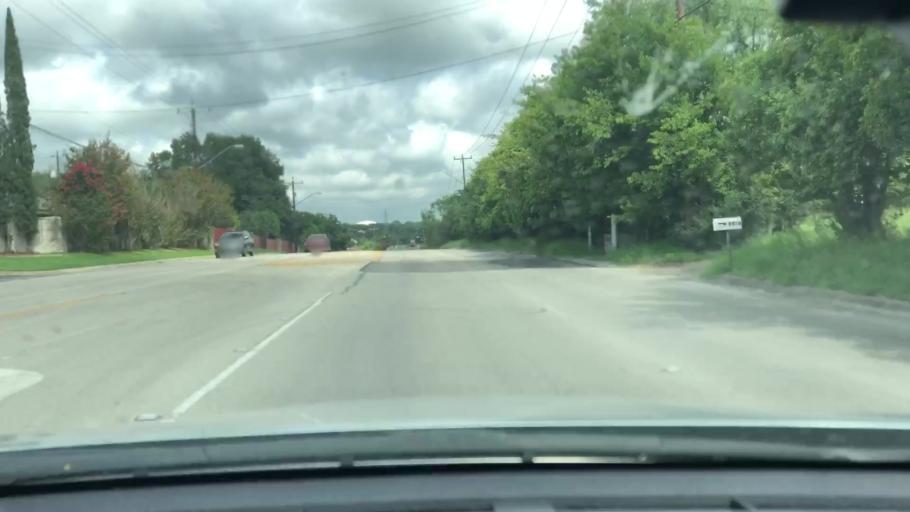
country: US
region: Texas
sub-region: Bexar County
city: Windcrest
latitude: 29.5245
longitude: -98.3692
